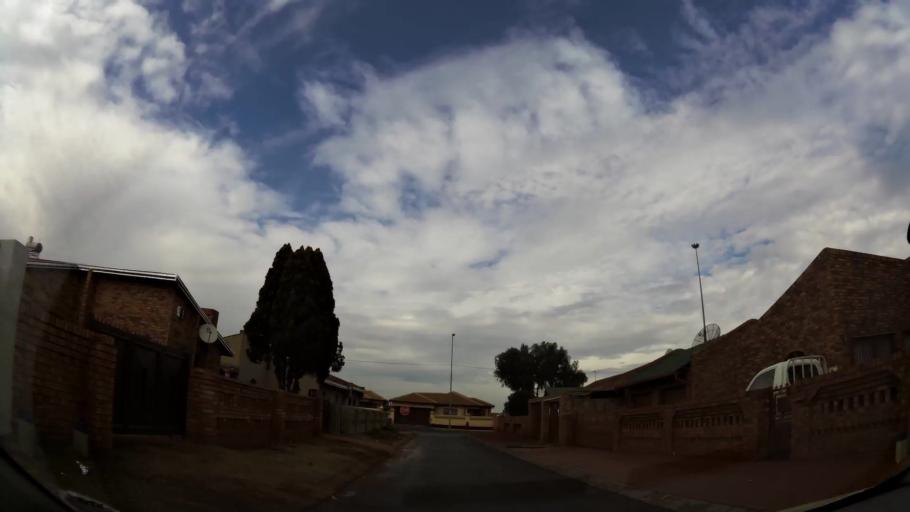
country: ZA
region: Gauteng
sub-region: Ekurhuleni Metropolitan Municipality
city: Germiston
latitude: -26.3304
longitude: 28.1916
